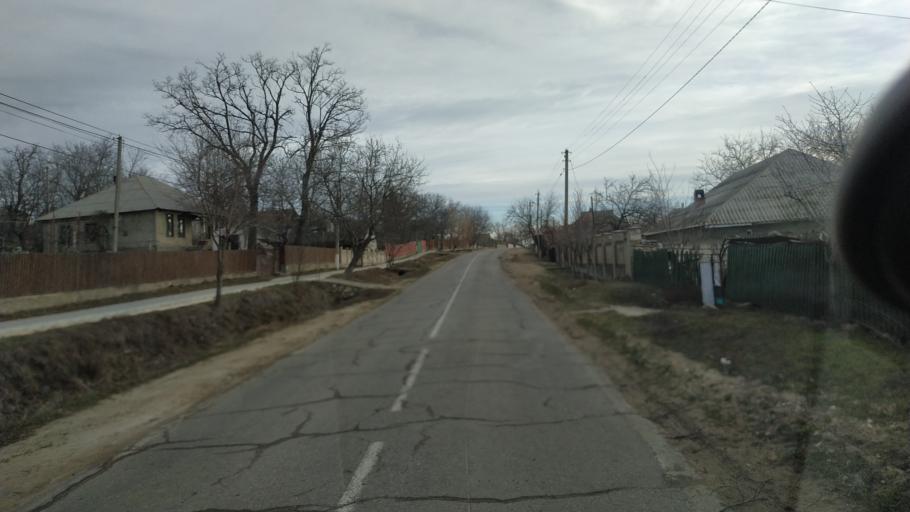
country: MD
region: Chisinau
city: Vadul lui Voda
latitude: 47.1473
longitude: 29.0785
